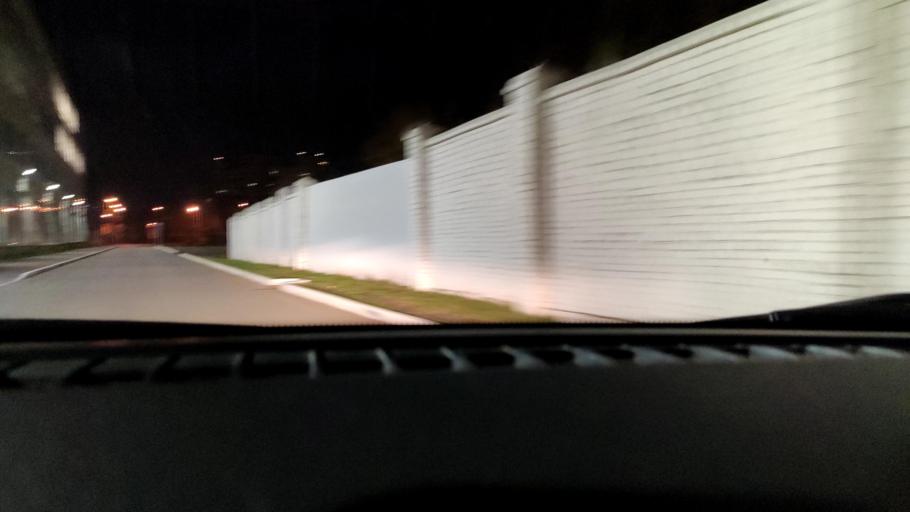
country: RU
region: Perm
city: Perm
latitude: 57.9918
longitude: 56.2081
